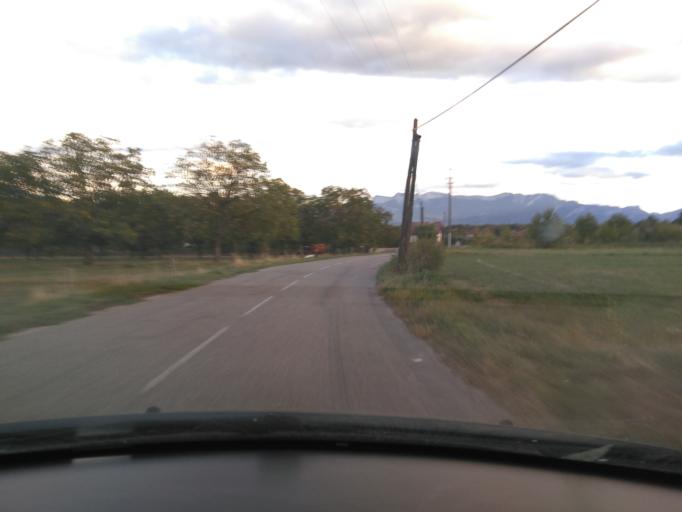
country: FR
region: Rhone-Alpes
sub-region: Departement de l'Isere
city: La Murette
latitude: 45.3747
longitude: 5.5240
